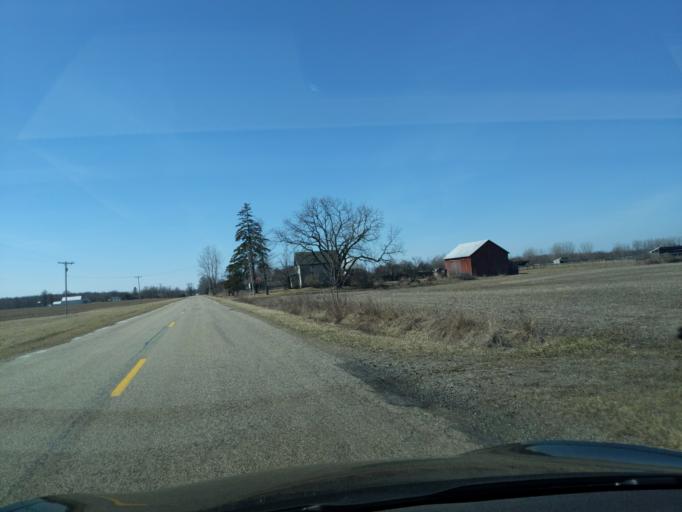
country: US
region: Michigan
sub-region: Ionia County
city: Portland
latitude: 42.7267
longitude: -84.9468
